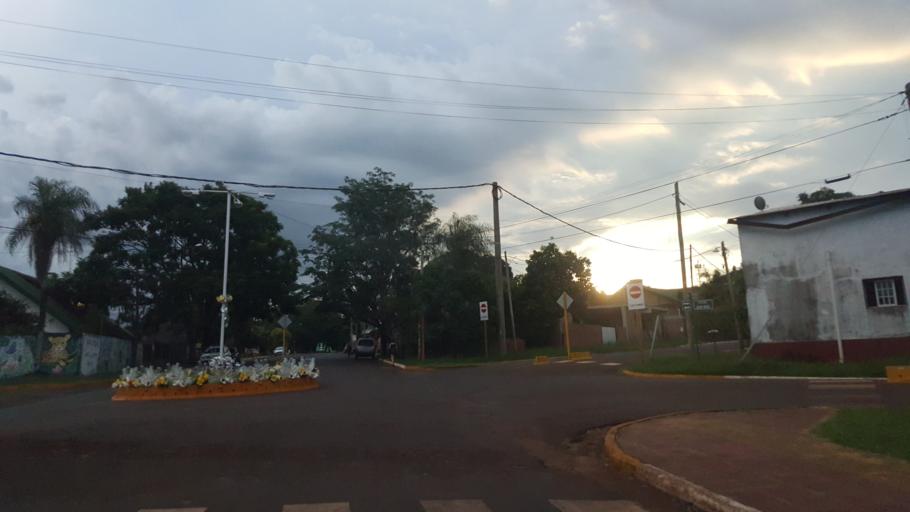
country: AR
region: Misiones
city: Jardin America
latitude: -27.0415
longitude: -55.2252
